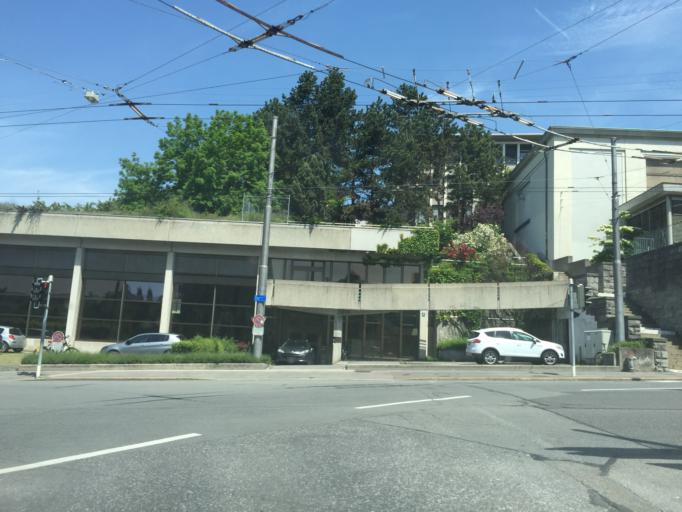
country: CH
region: Vaud
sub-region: Lausanne District
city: Lausanne
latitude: 46.5220
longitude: 6.6390
